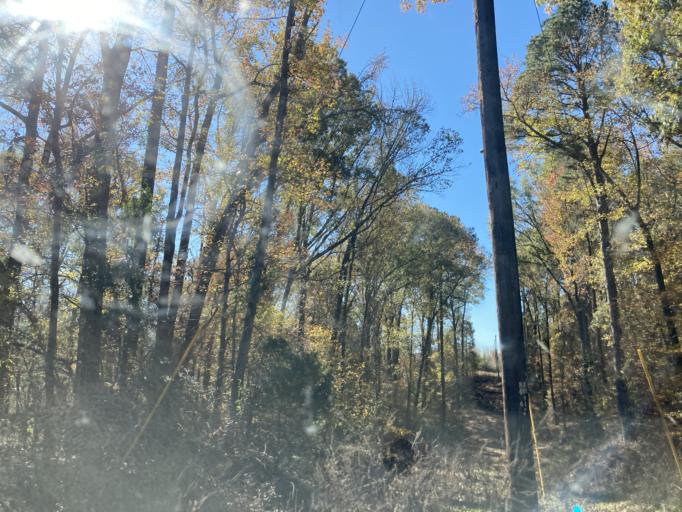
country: US
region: Mississippi
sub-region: Hinds County
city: Lynchburg
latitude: 32.5683
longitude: -90.5112
